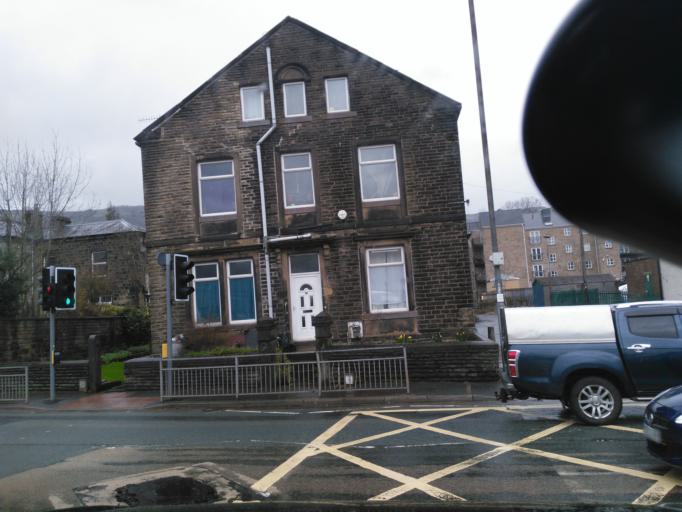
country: GB
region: England
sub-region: Calderdale
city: Mytholmroyd
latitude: 53.7309
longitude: -1.9838
